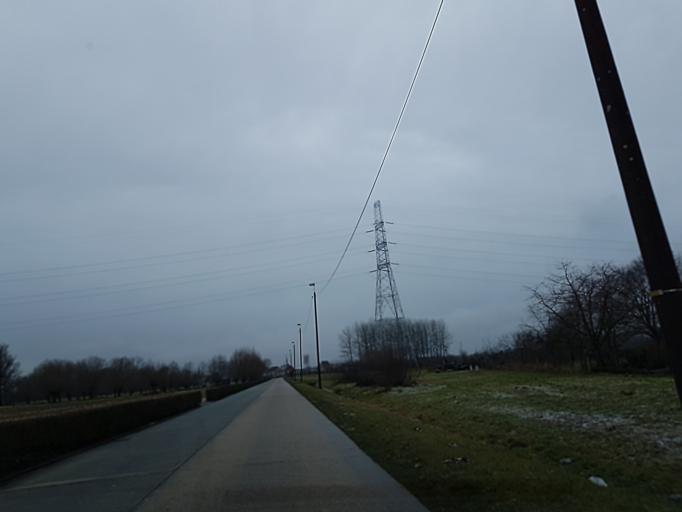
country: BE
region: Flanders
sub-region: Provincie Antwerpen
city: Sint-Amands
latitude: 51.0600
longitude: 4.2248
